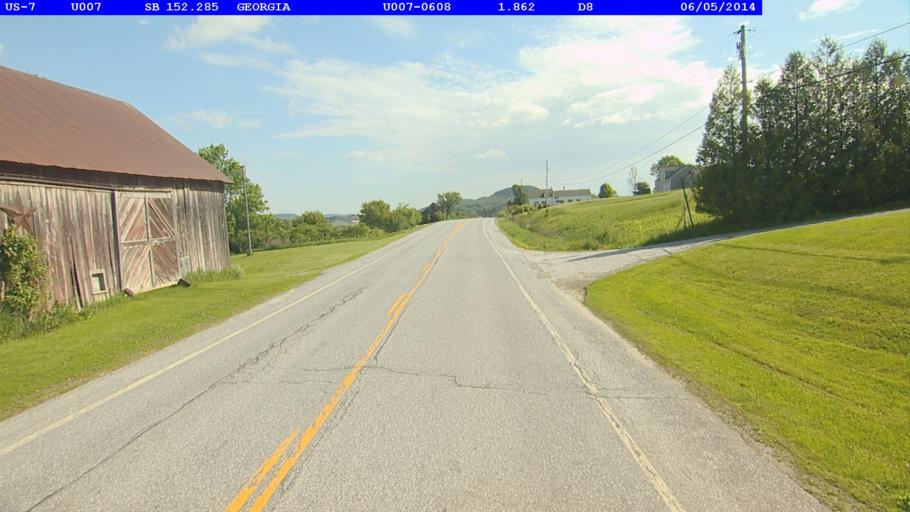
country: US
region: Vermont
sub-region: Chittenden County
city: Milton
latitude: 44.7054
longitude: -73.1040
